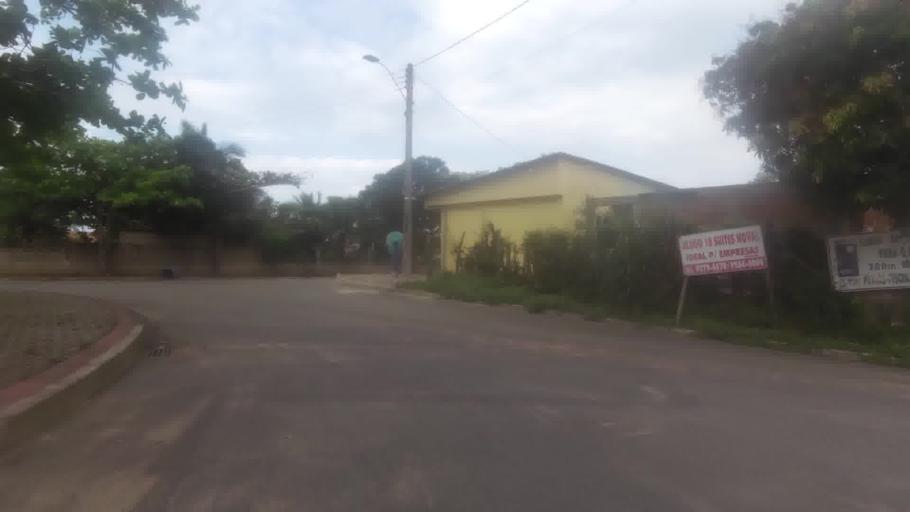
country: BR
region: Espirito Santo
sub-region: Piuma
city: Piuma
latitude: -20.7983
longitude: -40.5867
